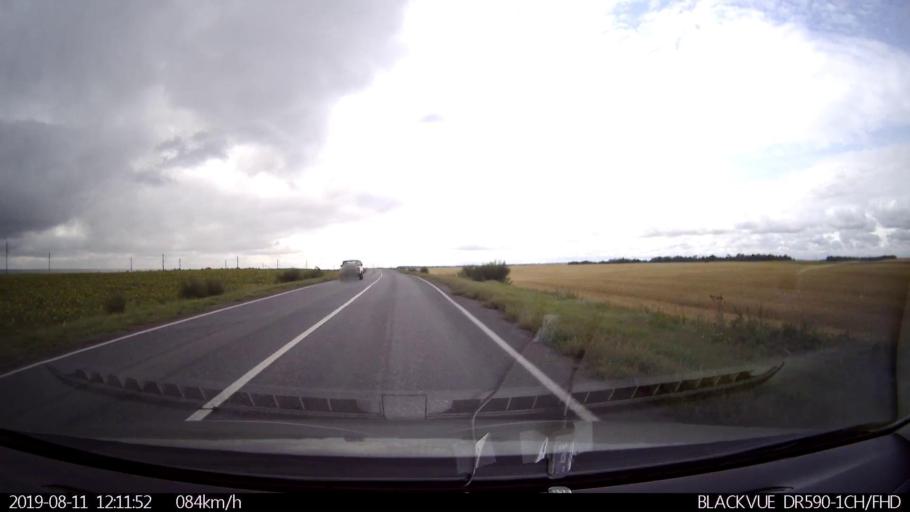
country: RU
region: Ulyanovsk
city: Silikatnyy
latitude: 53.9804
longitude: 47.9998
